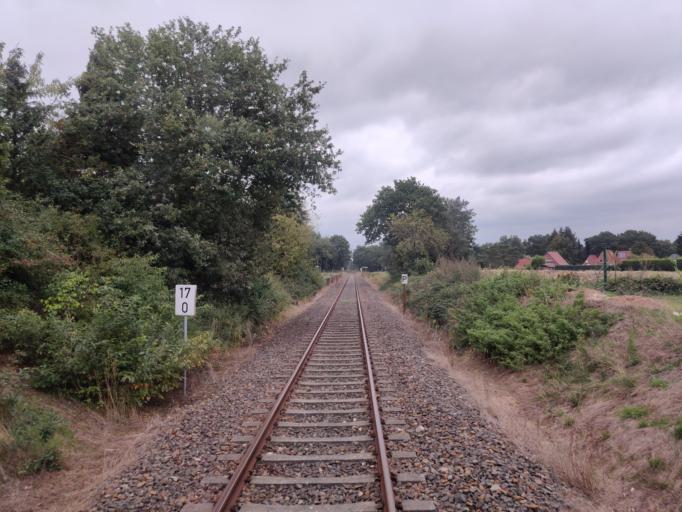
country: DE
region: Lower Saxony
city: Gnarrenburg
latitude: 53.3954
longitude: 9.0148
